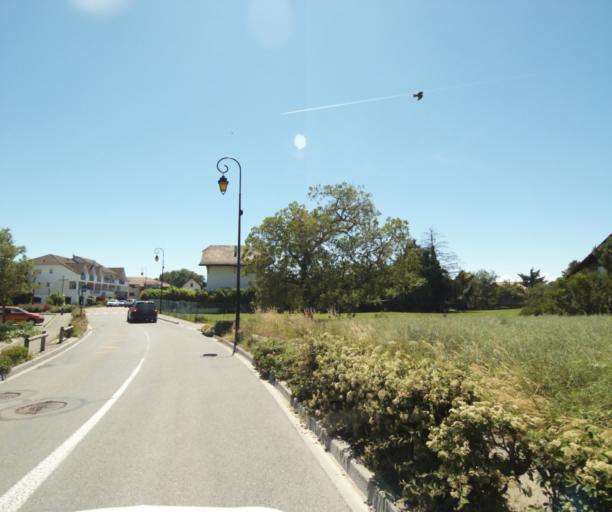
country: FR
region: Rhone-Alpes
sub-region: Departement de la Haute-Savoie
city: Veigy-Foncenex
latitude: 46.2655
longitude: 6.2527
